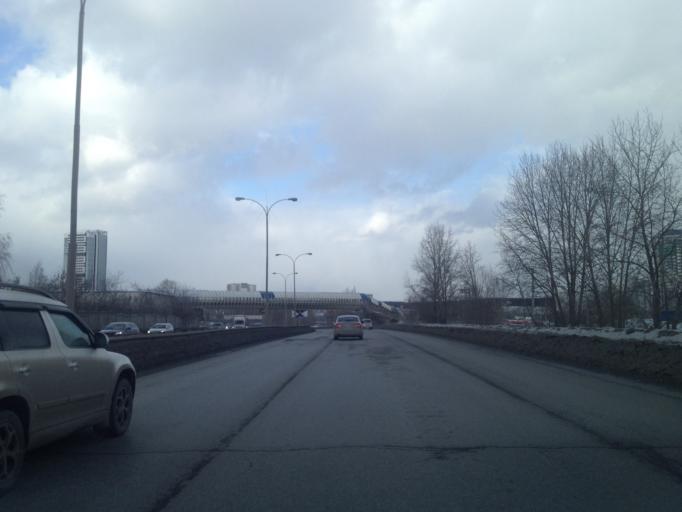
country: RU
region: Sverdlovsk
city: Yekaterinburg
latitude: 56.7908
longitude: 60.6379
